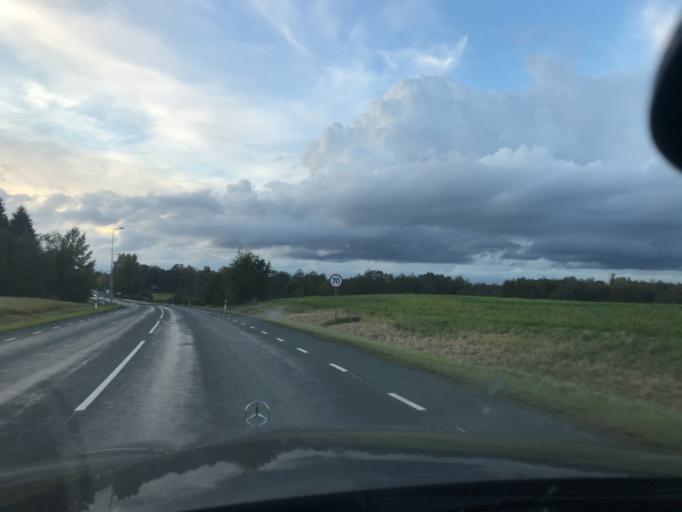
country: EE
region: Vorumaa
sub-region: Antsla vald
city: Vana-Antsla
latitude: 57.9248
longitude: 26.3403
